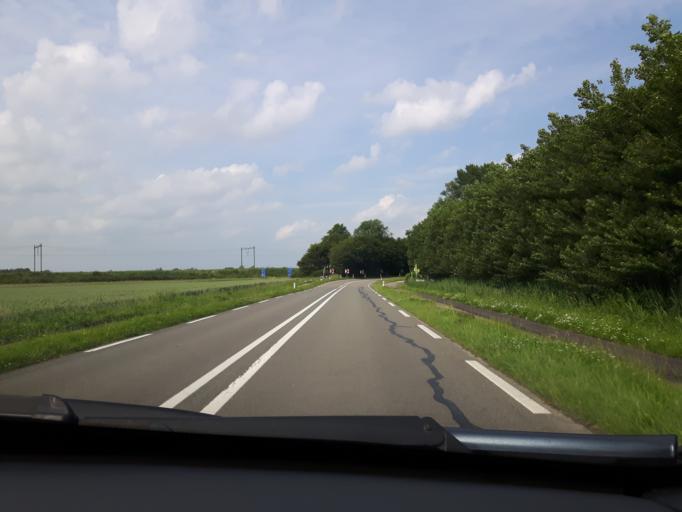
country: NL
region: Zeeland
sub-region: Gemeente Veere
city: Veere
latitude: 51.5017
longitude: 3.6966
